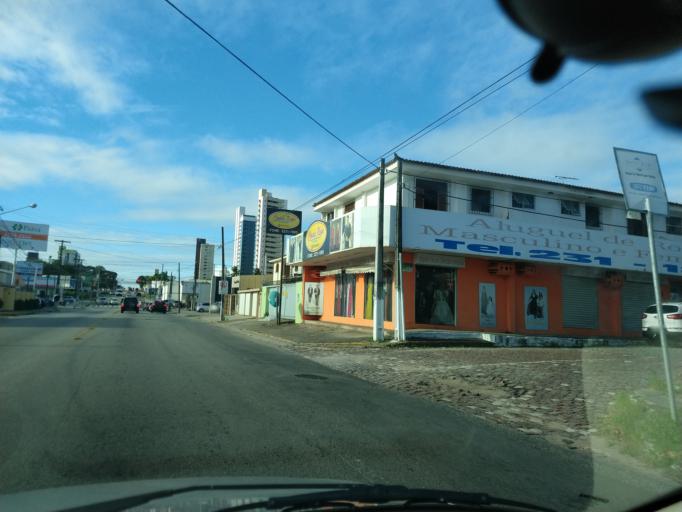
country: BR
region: Rio Grande do Norte
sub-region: Natal
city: Natal
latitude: -5.8228
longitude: -35.2197
